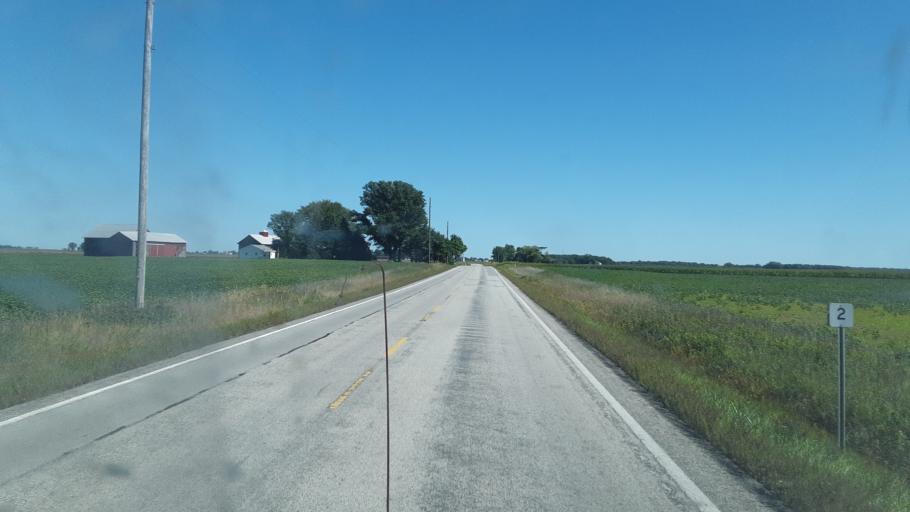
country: US
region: Ohio
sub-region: Huron County
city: Bellevue
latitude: 41.2102
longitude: -82.8034
